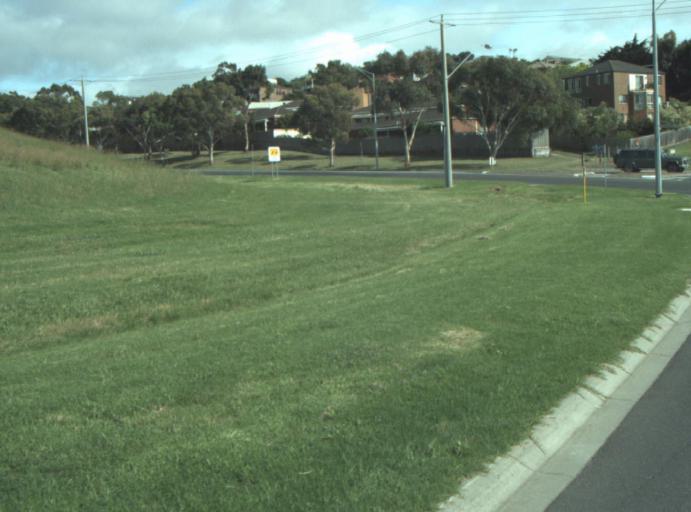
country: AU
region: Victoria
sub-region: Greater Geelong
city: Wandana Heights
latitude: -38.1697
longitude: 144.3097
